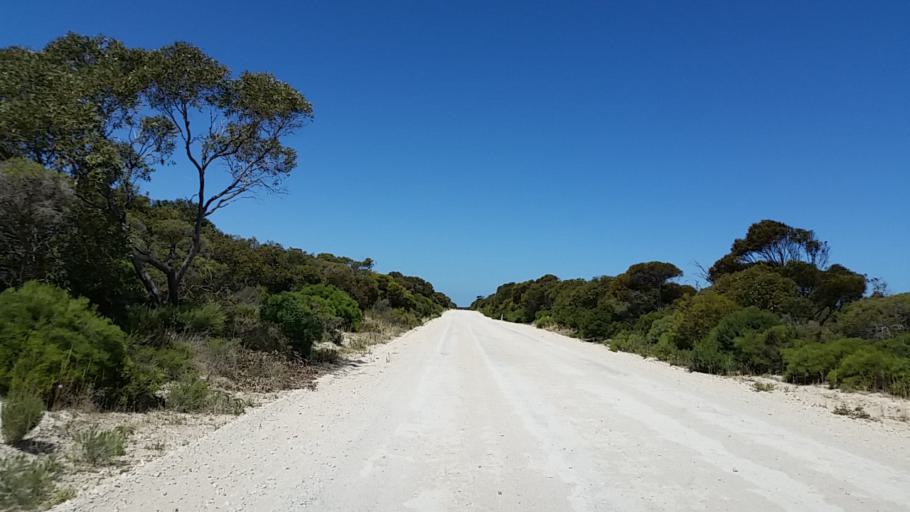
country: AU
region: South Australia
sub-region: Yorke Peninsula
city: Honiton
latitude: -35.2161
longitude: 137.0079
